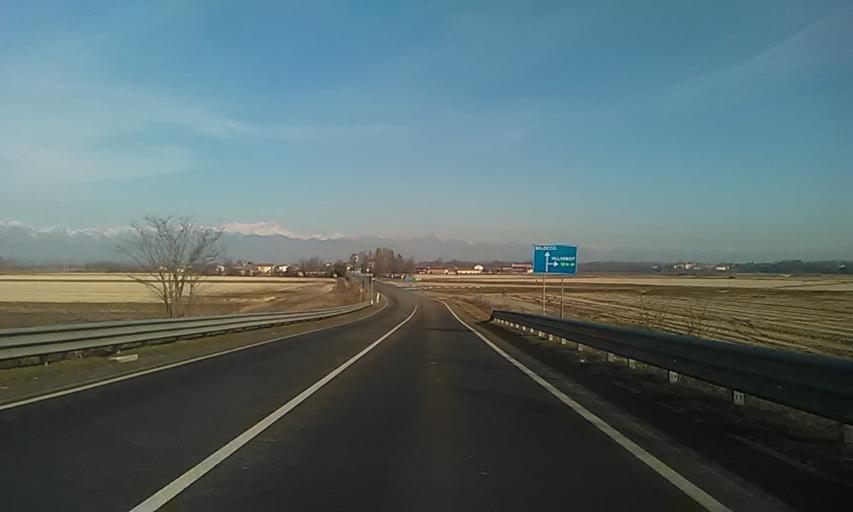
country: IT
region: Piedmont
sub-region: Provincia di Vercelli
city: Balocco
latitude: 45.4484
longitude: 8.2852
